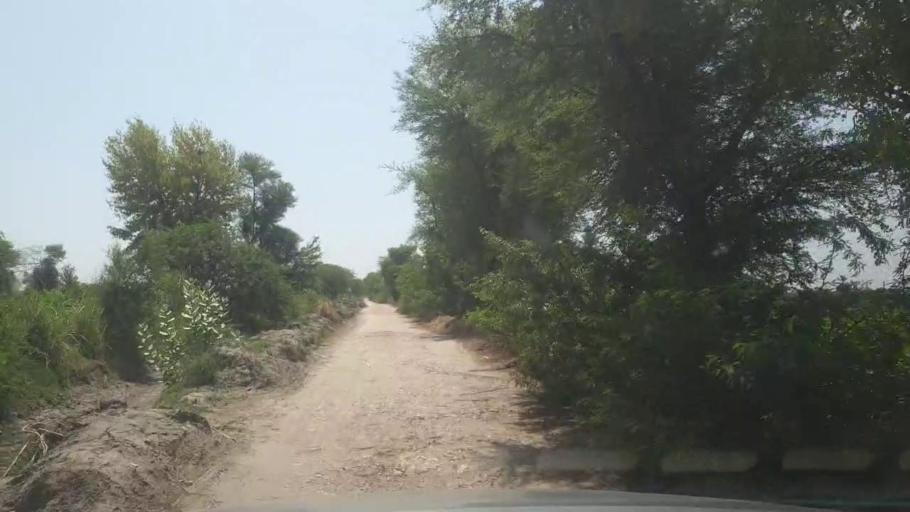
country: PK
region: Sindh
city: Khairpur
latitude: 27.3639
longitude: 69.0263
